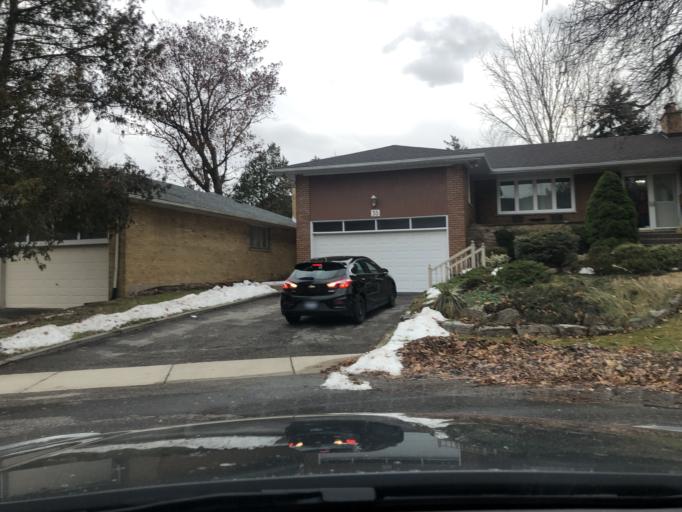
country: CA
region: Ontario
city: Etobicoke
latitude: 43.6947
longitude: -79.5246
